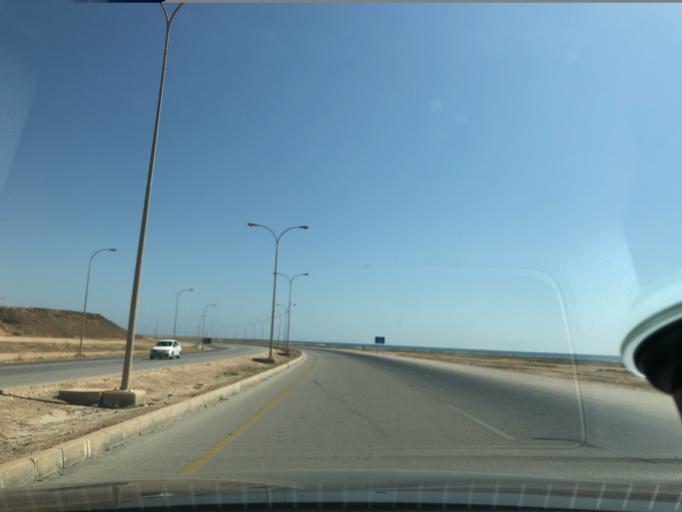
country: OM
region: Zufar
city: Salalah
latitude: 17.0384
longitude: 54.3423
